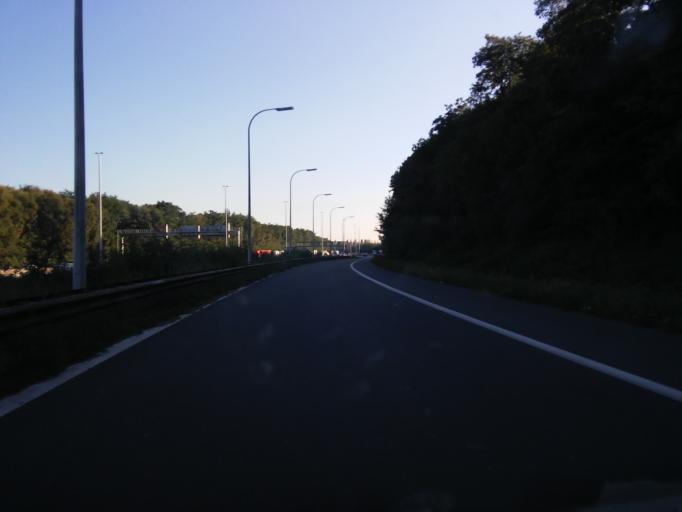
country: BE
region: Flanders
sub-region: Provincie Antwerpen
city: Edegem
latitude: 51.1698
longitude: 4.4132
